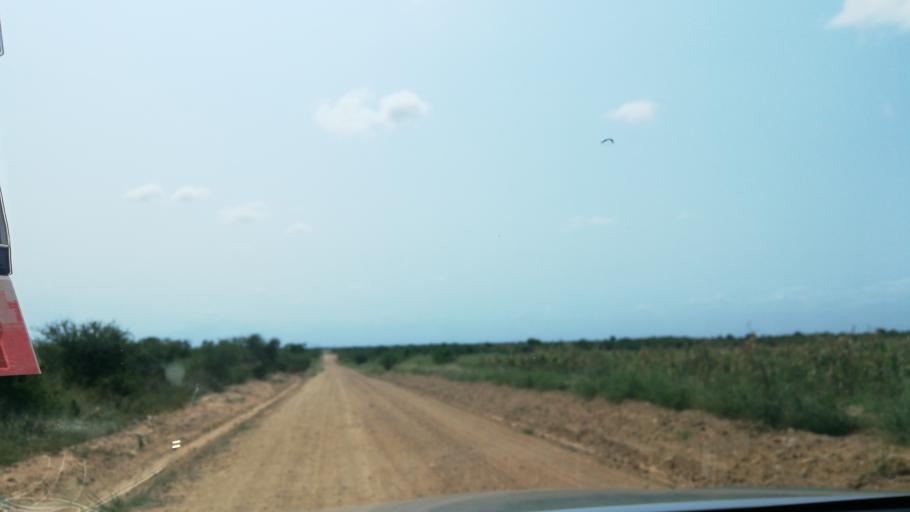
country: MZ
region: Maputo
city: Matola
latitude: -26.0823
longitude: 32.3914
